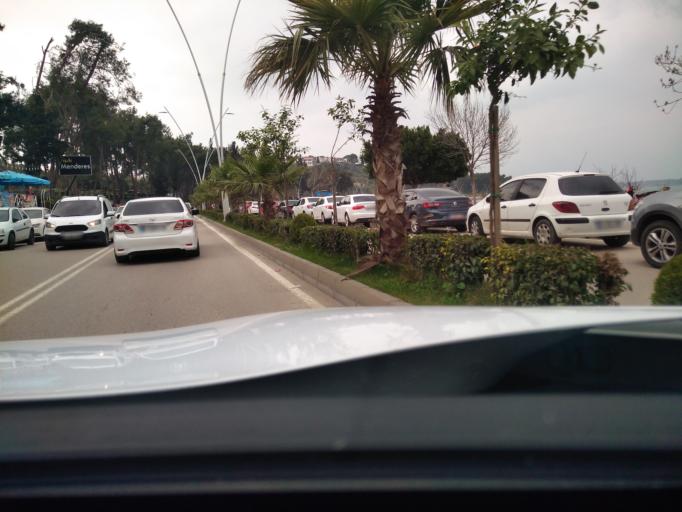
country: TR
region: Adana
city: Adana
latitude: 37.0502
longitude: 35.3078
